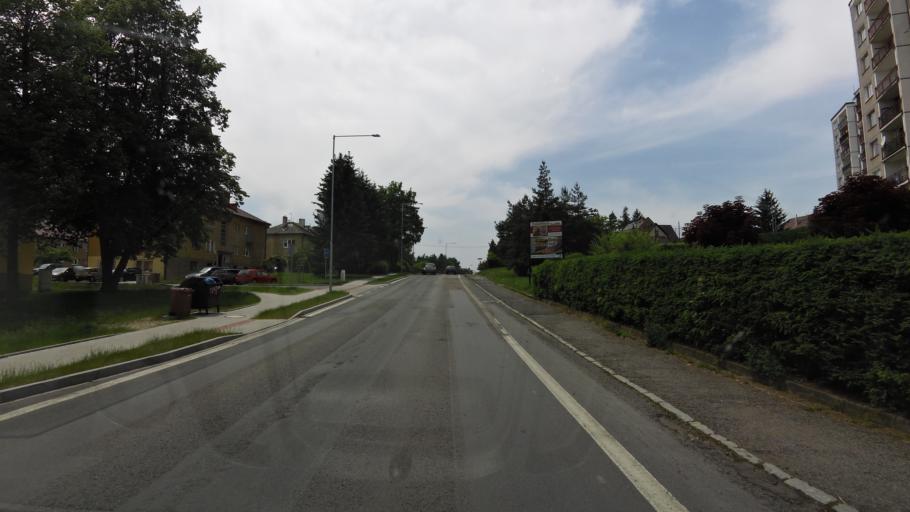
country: CZ
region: Plzensky
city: Holoubkov
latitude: 49.7747
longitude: 13.6901
